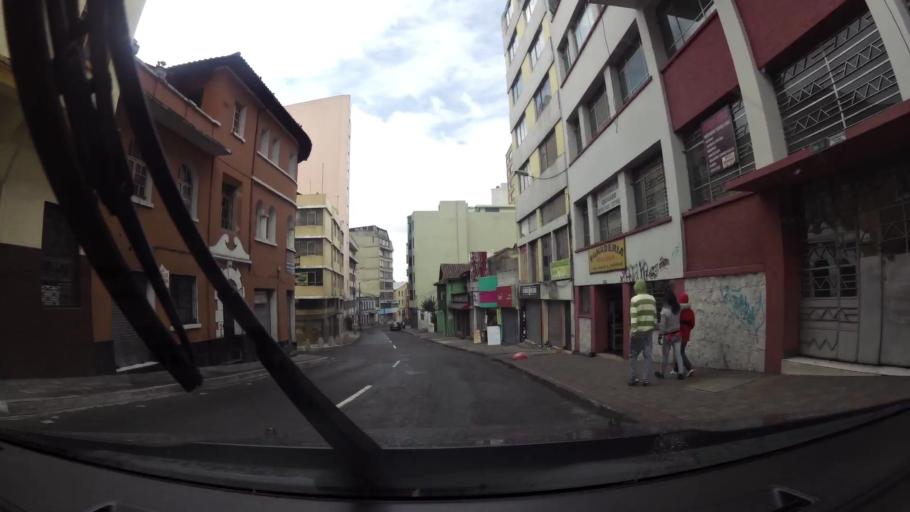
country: EC
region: Pichincha
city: Quito
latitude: -0.2124
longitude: -78.5012
